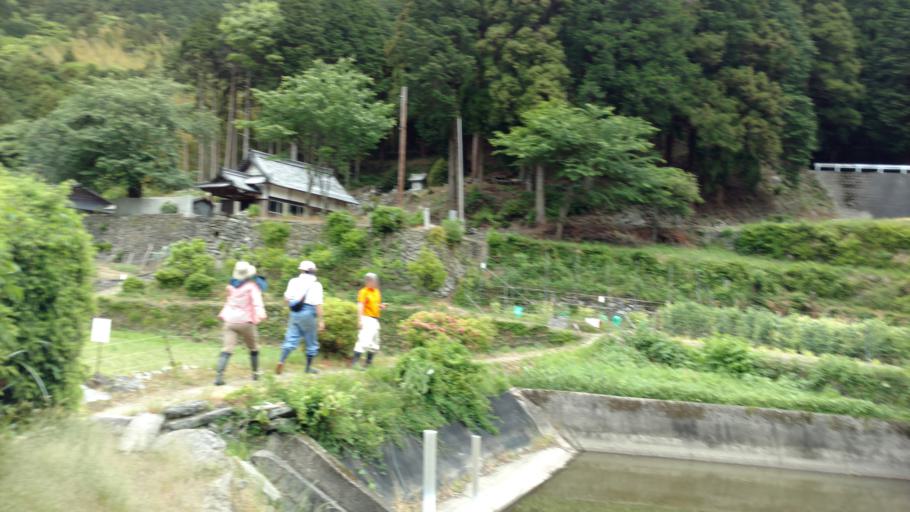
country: JP
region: Ehime
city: Saijo
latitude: 33.8662
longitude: 133.1984
